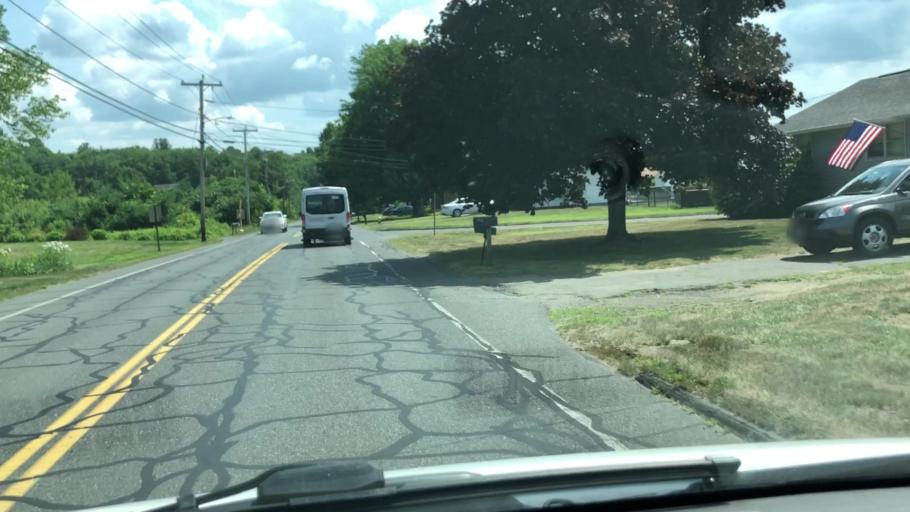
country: US
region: Massachusetts
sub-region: Hampshire County
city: Easthampton
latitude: 42.2993
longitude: -72.6734
